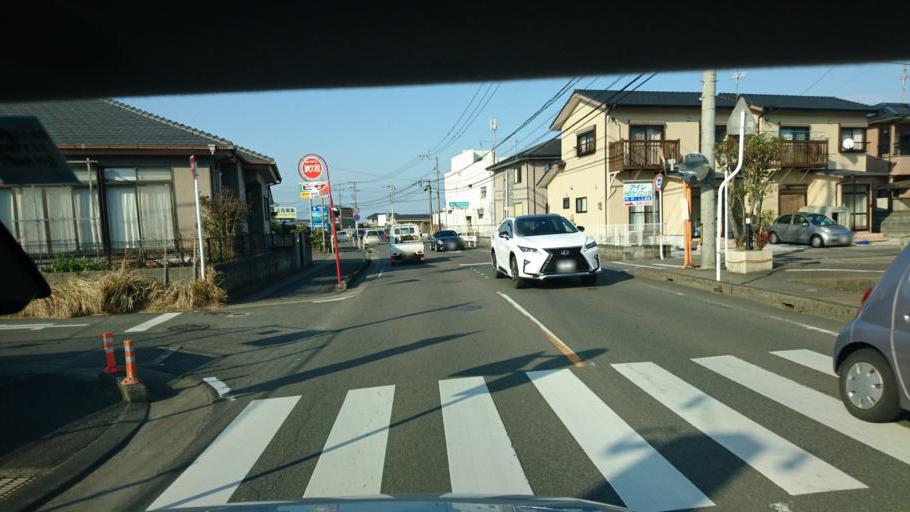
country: JP
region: Miyazaki
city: Miyazaki-shi
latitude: 31.9765
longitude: 131.4404
